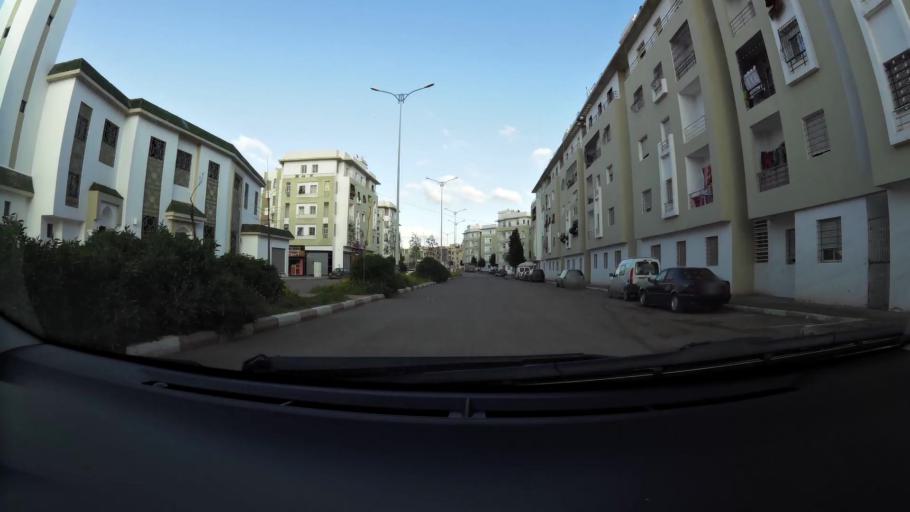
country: MA
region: Chaouia-Ouardigha
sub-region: Settat Province
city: Settat
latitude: 32.9979
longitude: -7.6345
